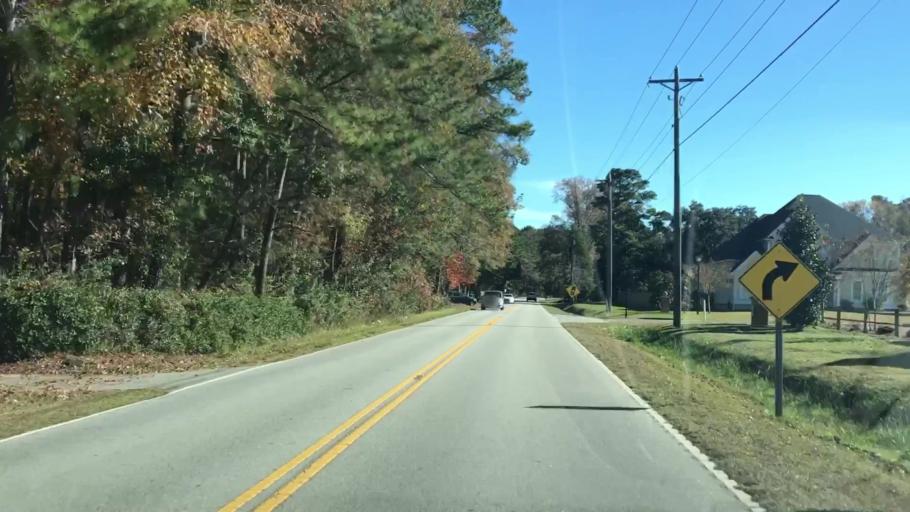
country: US
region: South Carolina
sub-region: Dorchester County
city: Summerville
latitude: 33.0208
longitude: -80.2246
